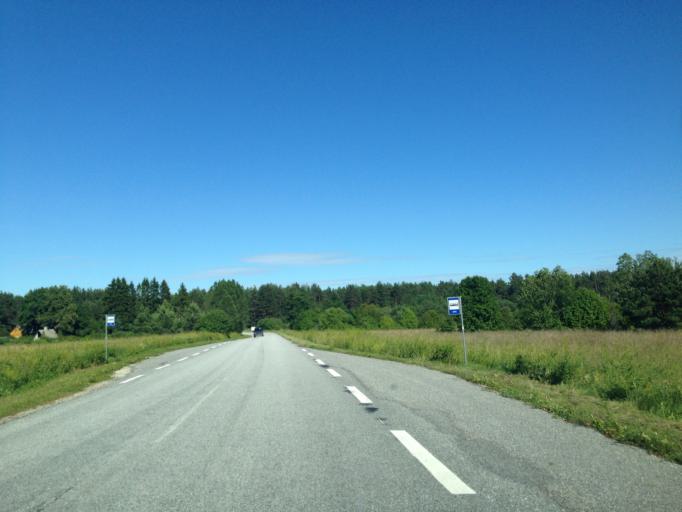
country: EE
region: Harju
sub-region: Raasiku vald
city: Raasiku
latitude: 59.4592
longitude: 25.2271
